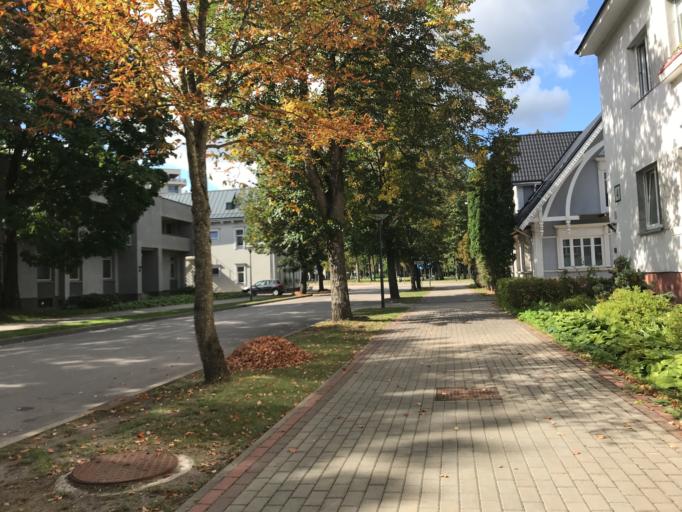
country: LT
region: Alytaus apskritis
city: Druskininkai
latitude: 54.0207
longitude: 23.9729
